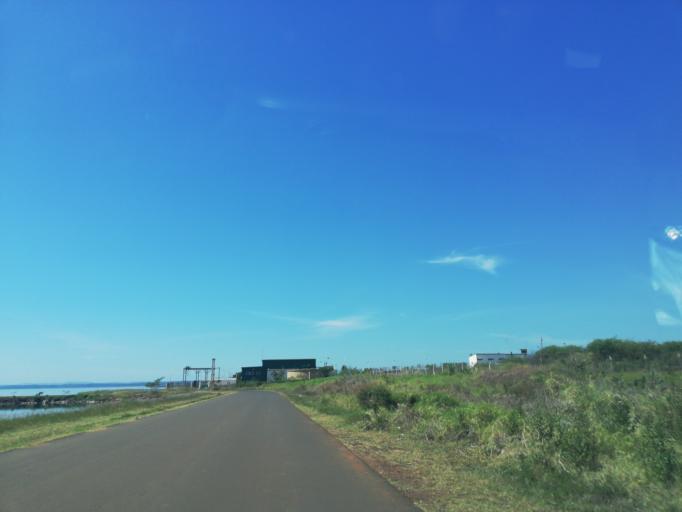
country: AR
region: Misiones
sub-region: Departamento de Capital
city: Posadas
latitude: -27.4245
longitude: -55.8716
